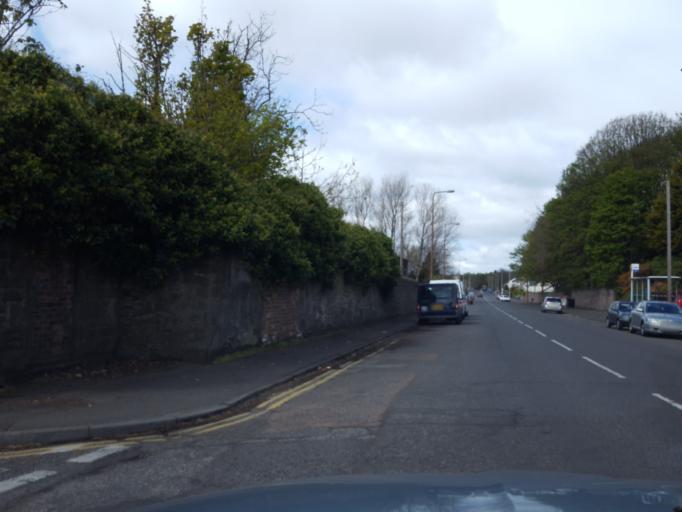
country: GB
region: Scotland
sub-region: Dundee City
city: Dundee
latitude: 56.4751
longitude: -3.0186
